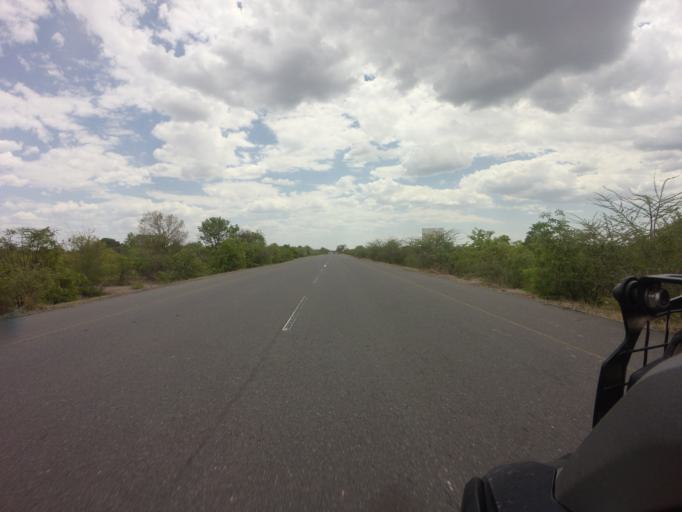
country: AO
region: Huila
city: Lubango
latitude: -15.5156
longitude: 14.0459
